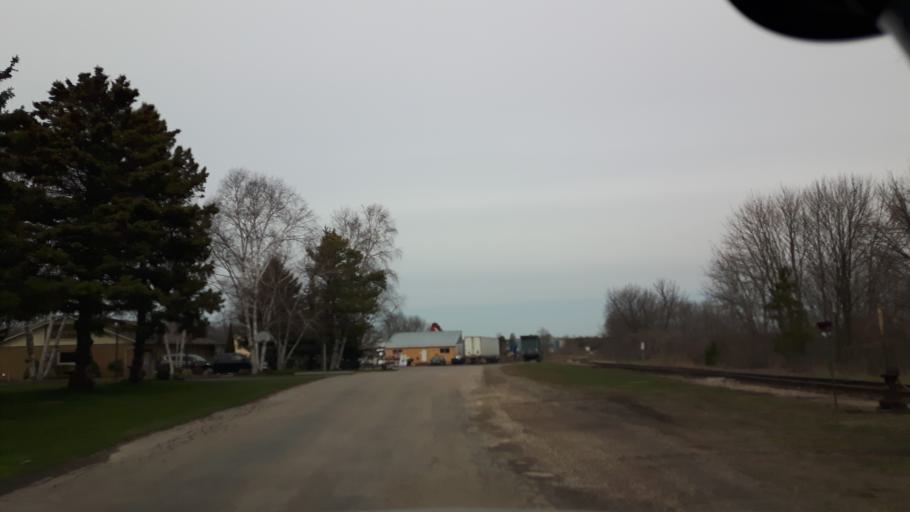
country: CA
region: Ontario
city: Goderich
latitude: 43.7447
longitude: -81.7007
